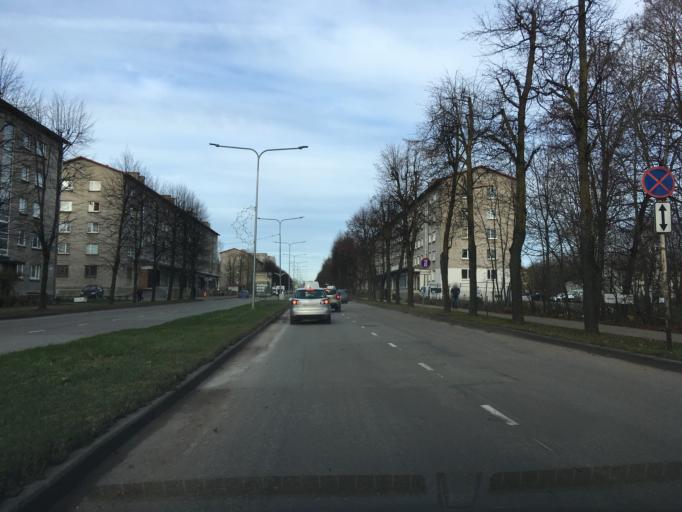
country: EE
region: Ida-Virumaa
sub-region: Narva linn
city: Narva
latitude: 59.3746
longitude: 28.1821
